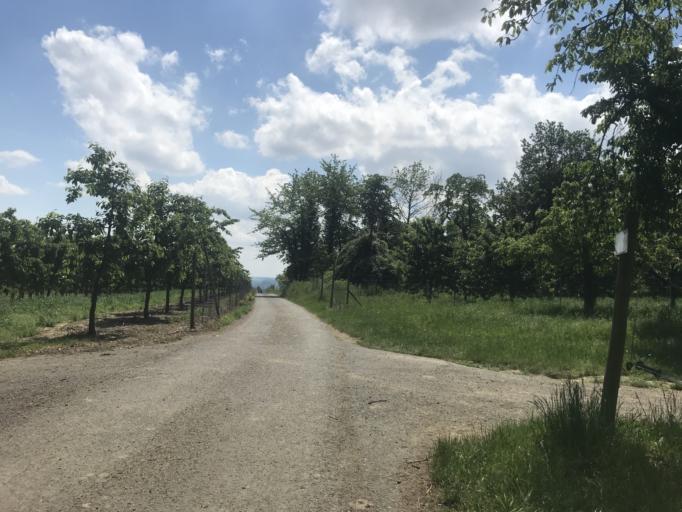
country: DE
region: Hesse
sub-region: Regierungsbezirk Darmstadt
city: Walluf
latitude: 50.0714
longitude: 8.1571
